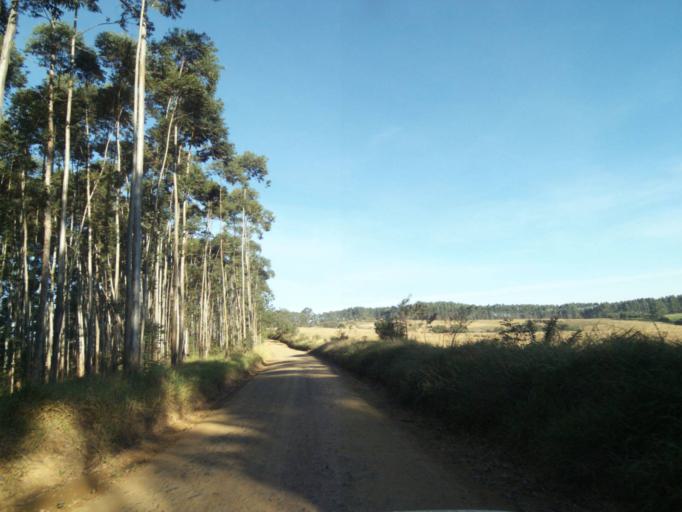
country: BR
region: Parana
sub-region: Tibagi
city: Tibagi
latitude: -24.5427
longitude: -50.6237
